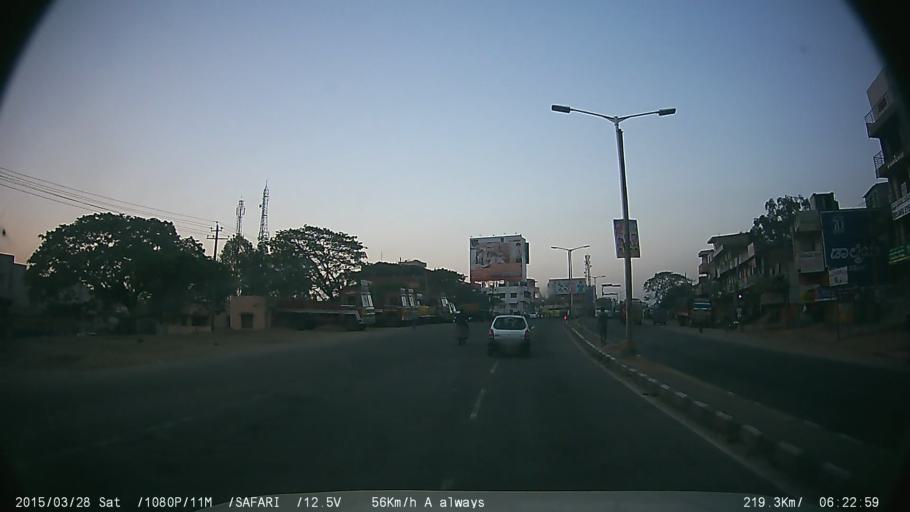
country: IN
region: Karnataka
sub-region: Ramanagara
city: Ramanagaram
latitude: 12.7241
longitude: 77.2751
